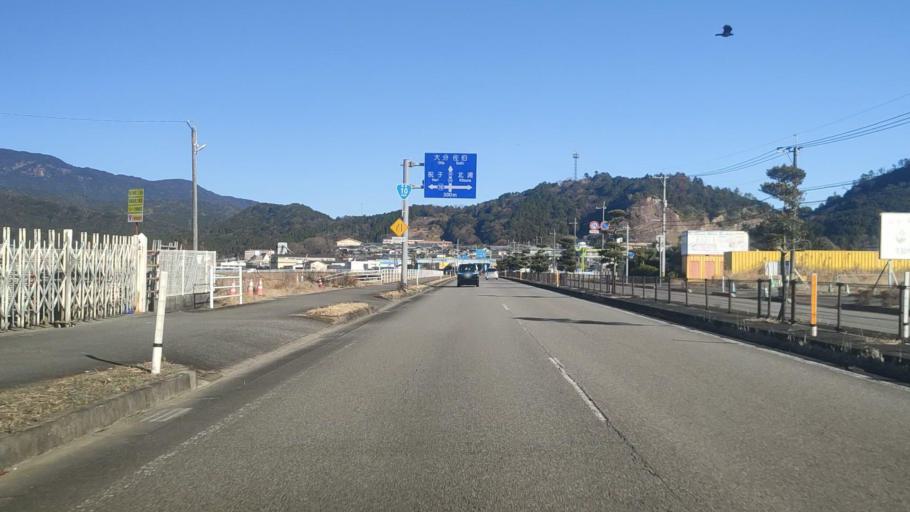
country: JP
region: Miyazaki
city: Nobeoka
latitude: 32.6068
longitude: 131.6830
